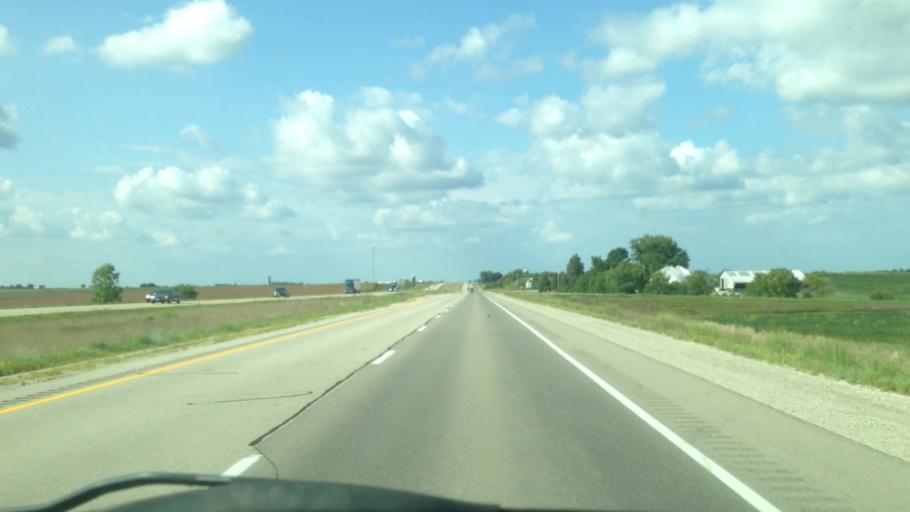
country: US
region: Iowa
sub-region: Henry County
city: Mount Pleasant
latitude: 40.7971
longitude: -91.5642
